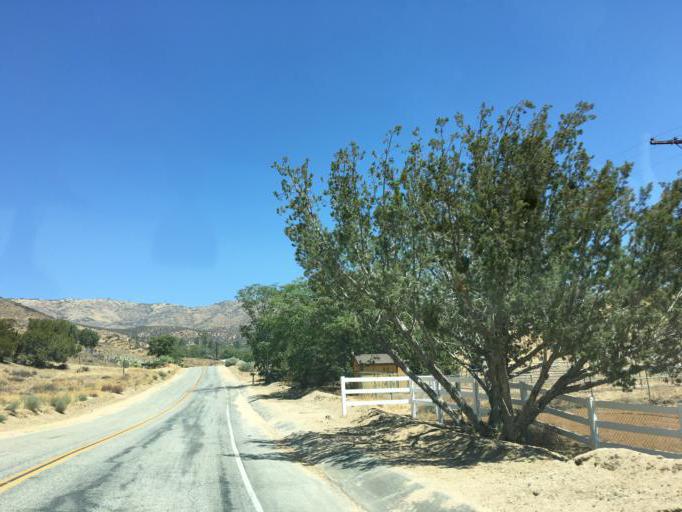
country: US
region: California
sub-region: Los Angeles County
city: Acton
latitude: 34.5128
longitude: -118.2157
